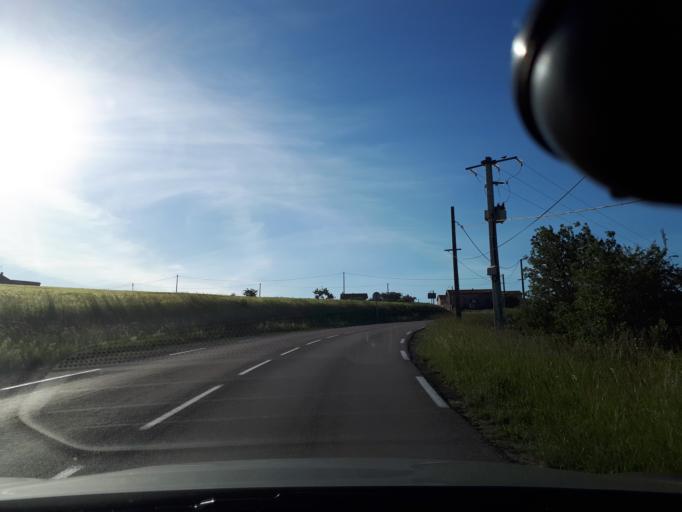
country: FR
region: Rhone-Alpes
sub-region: Departement de la Loire
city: Saint-Joseph
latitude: 45.5441
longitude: 4.6313
